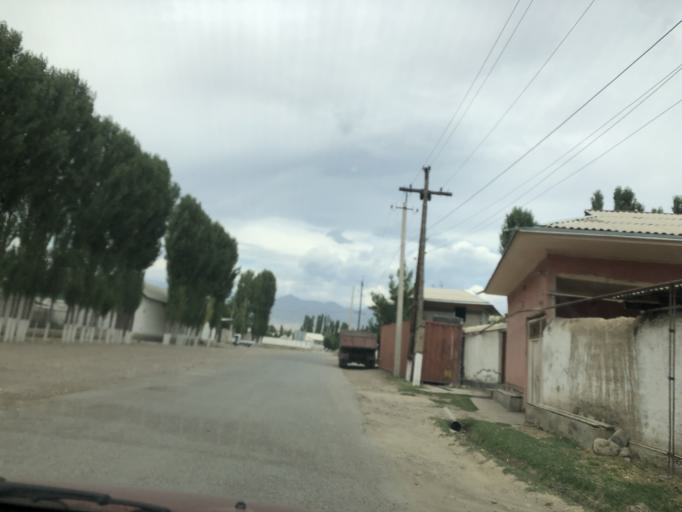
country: UZ
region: Namangan
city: Pop Shahri
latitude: 41.0117
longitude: 71.0876
